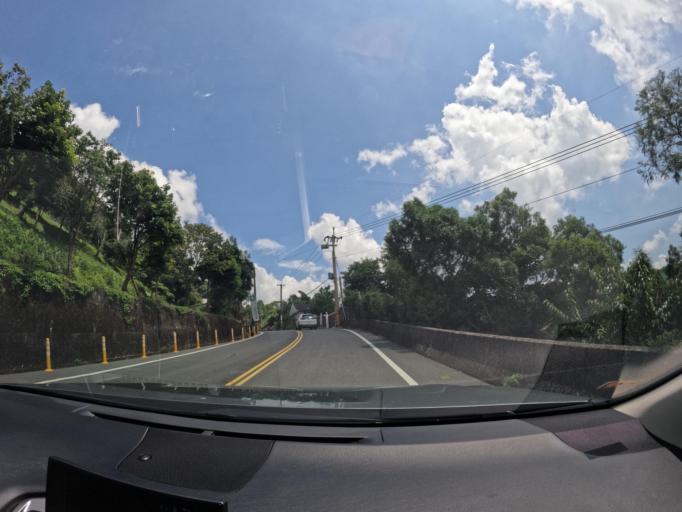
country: TW
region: Taiwan
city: Fengyuan
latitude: 24.3861
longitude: 120.8209
